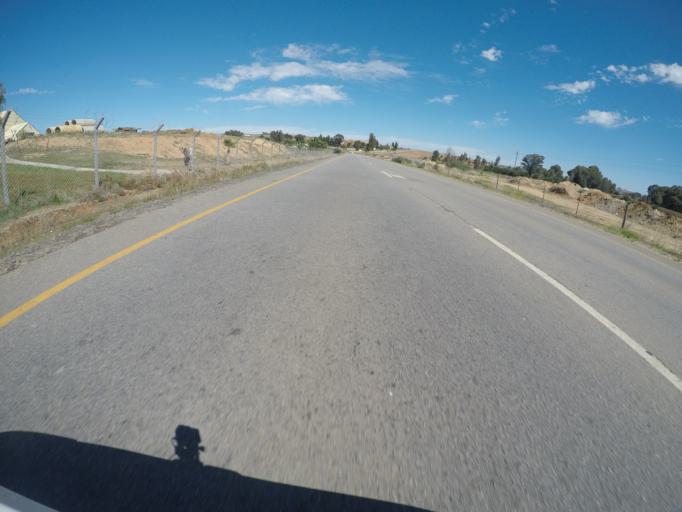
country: ZA
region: Western Cape
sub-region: West Coast District Municipality
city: Malmesbury
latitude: -33.4764
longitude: 18.7163
